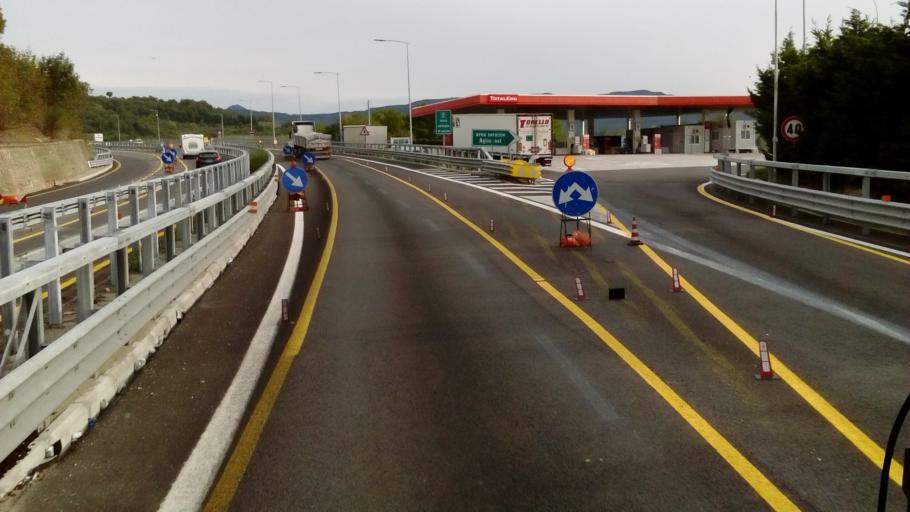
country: IT
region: Tuscany
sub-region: Province of Florence
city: Barberino di Mugello
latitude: 44.0289
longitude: 11.2250
